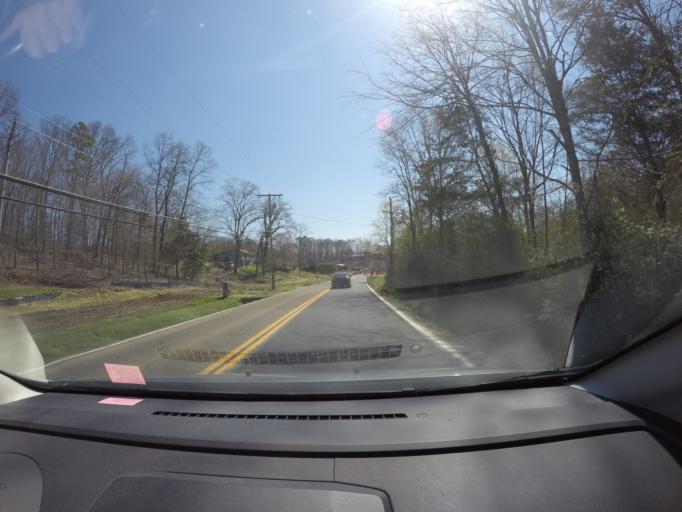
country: US
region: Tennessee
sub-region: Hamilton County
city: Collegedale
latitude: 35.0675
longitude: -85.0832
